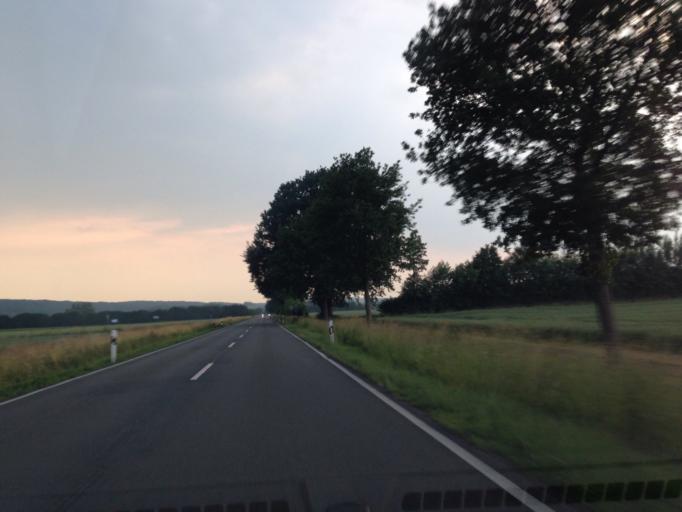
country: DE
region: North Rhine-Westphalia
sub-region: Regierungsbezirk Munster
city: Havixbeck
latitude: 51.9669
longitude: 7.4449
